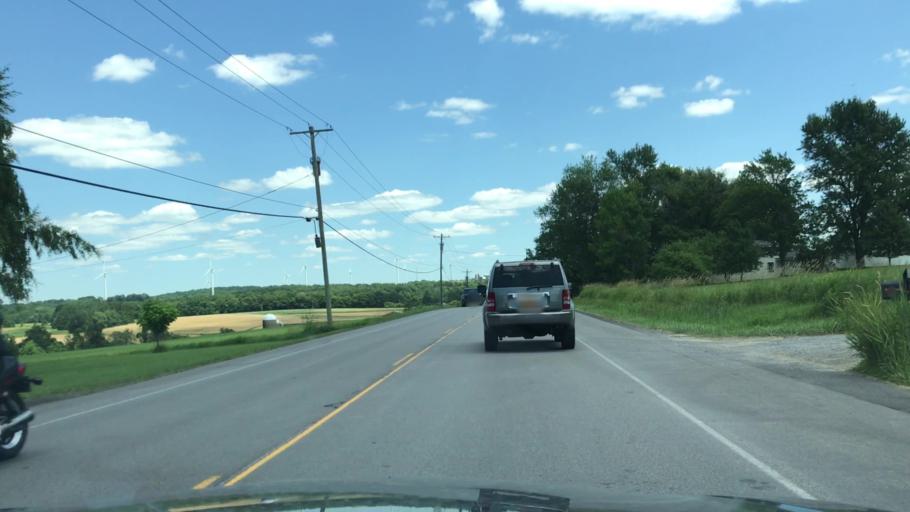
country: US
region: New York
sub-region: Erie County
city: Alden
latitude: 42.7696
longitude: -78.4547
